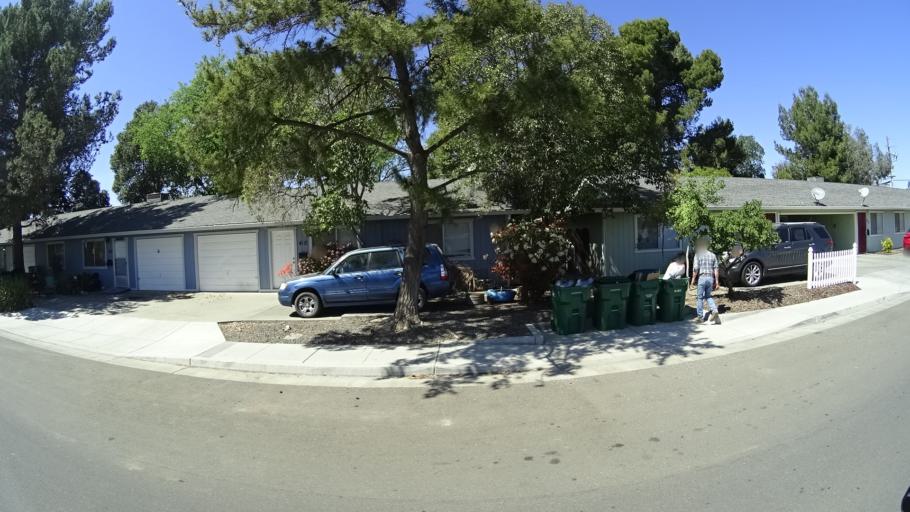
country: US
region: California
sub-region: Glenn County
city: Orland
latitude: 39.7504
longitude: -122.1782
